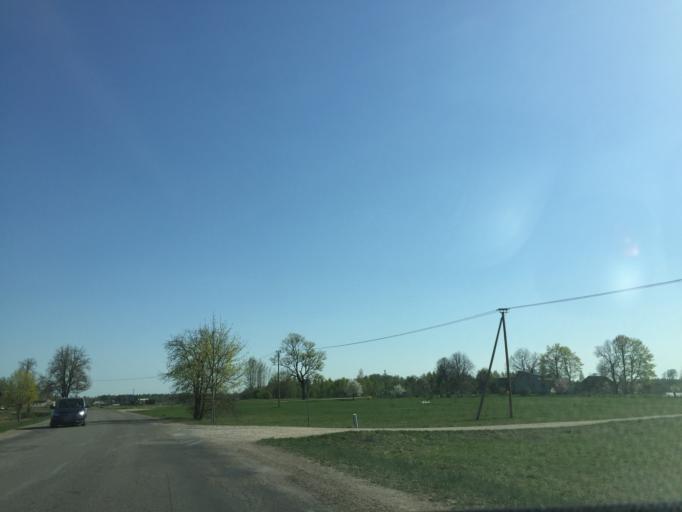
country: LV
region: Malpils
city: Malpils
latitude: 56.8958
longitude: 24.9285
